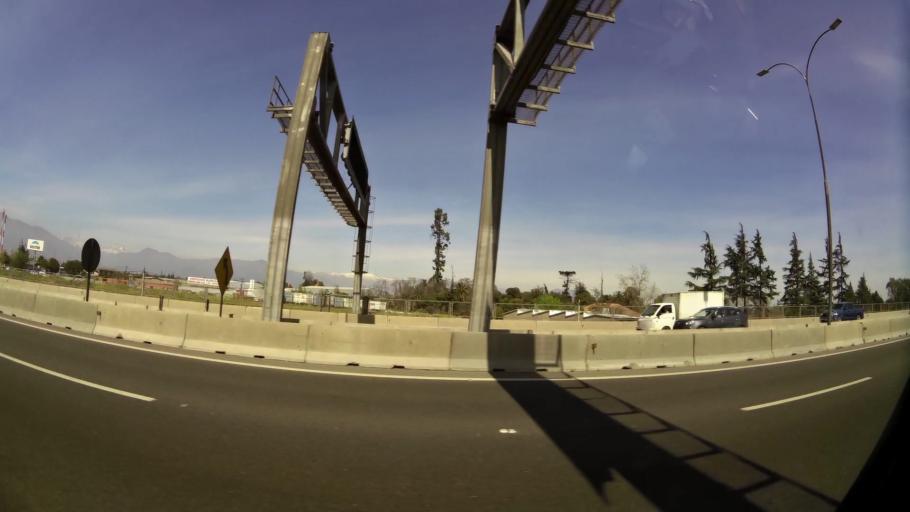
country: CL
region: Santiago Metropolitan
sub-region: Provincia de Maipo
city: San Bernardo
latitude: -33.5434
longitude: -70.6899
